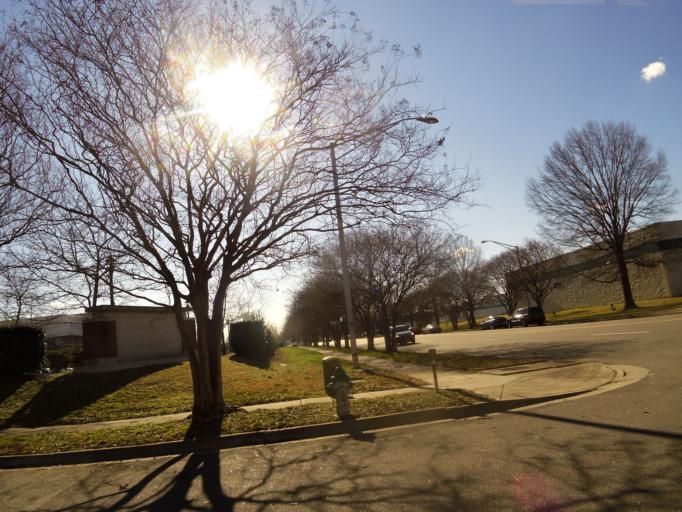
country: US
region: Virginia
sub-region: City of Portsmouth
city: Portsmouth
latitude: 36.8285
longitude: -76.3005
